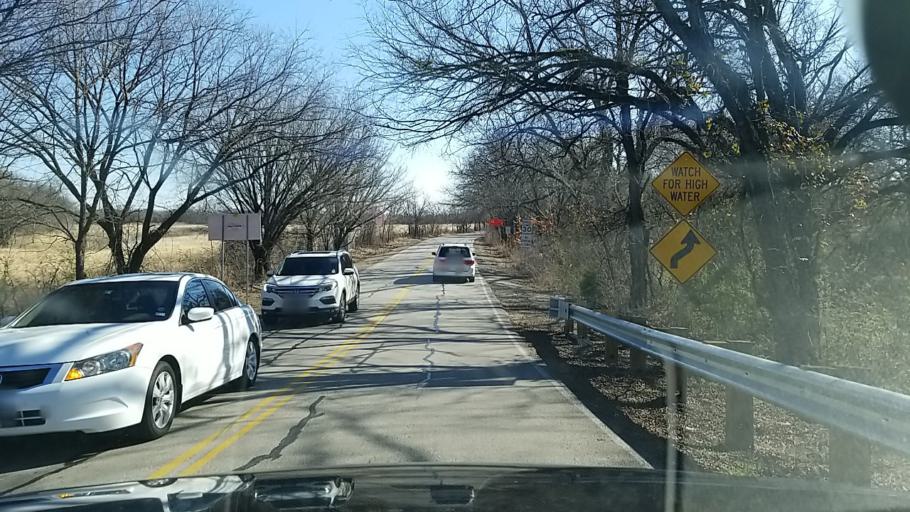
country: US
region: Texas
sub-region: Denton County
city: Argyle
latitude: 33.1518
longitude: -97.1417
